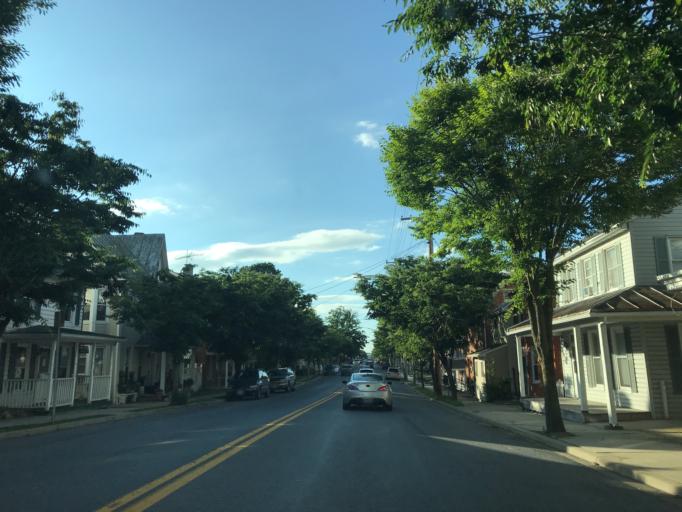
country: US
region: Maryland
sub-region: Carroll County
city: Manchester
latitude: 39.6571
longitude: -76.8825
